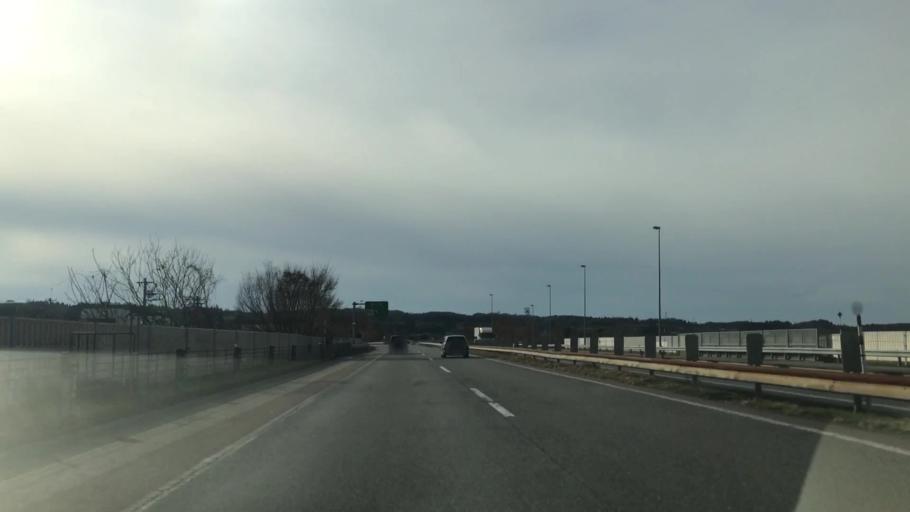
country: JP
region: Toyama
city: Kuragaki-kosugi
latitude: 36.6816
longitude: 137.1370
